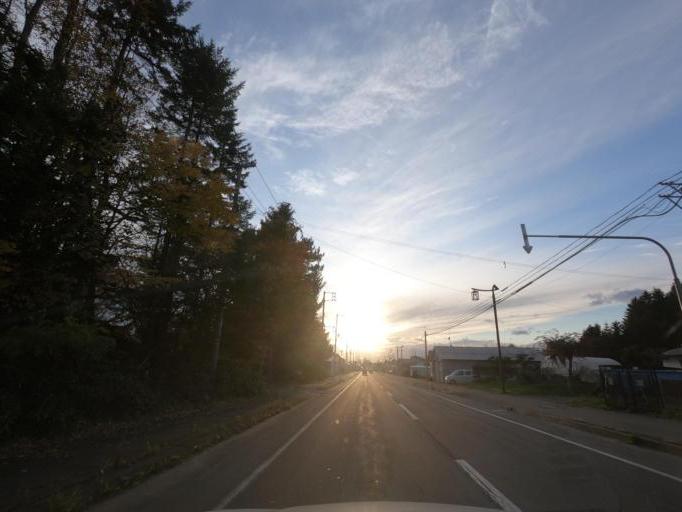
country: JP
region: Hokkaido
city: Obihiro
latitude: 42.5659
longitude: 143.3087
